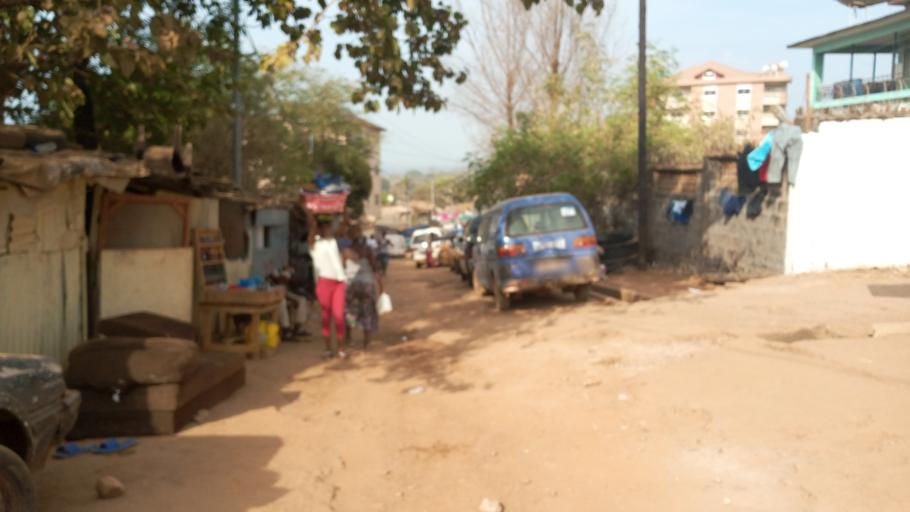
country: SL
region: Western Area
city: Freetown
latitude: 8.4824
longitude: -13.2604
